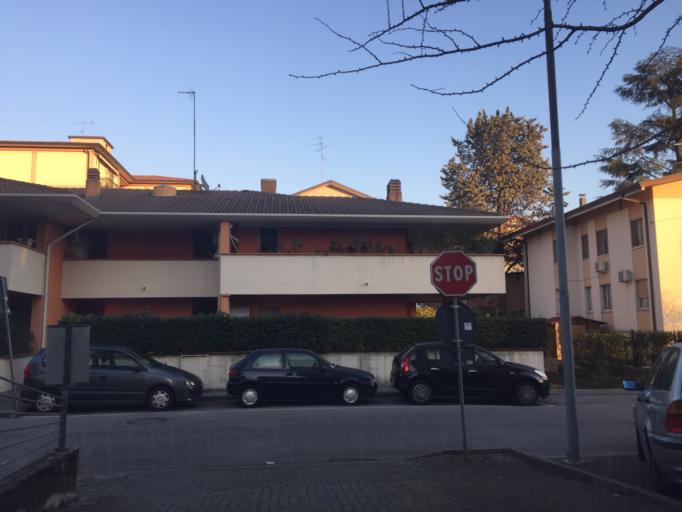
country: IT
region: Friuli Venezia Giulia
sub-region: Provincia di Pordenone
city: Sacile
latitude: 45.9492
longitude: 12.4972
